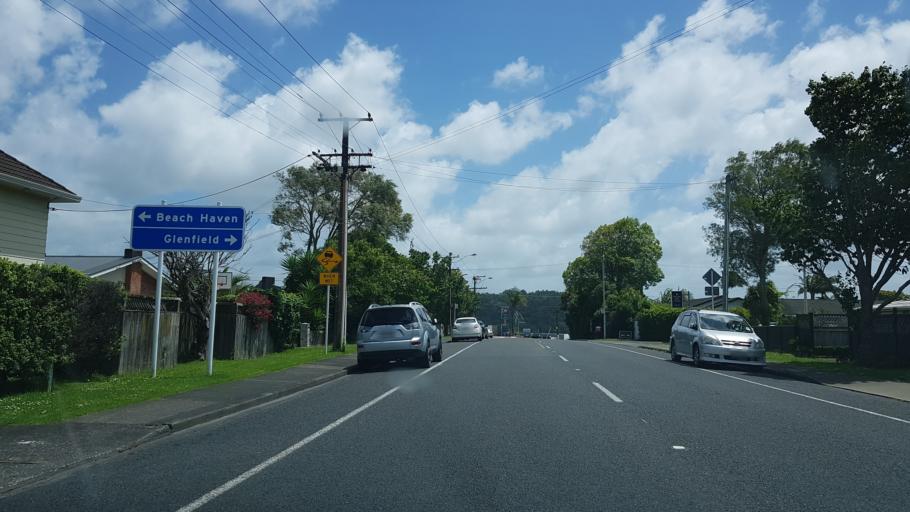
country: NZ
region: Auckland
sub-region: Auckland
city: North Shore
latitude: -36.7892
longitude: 174.7000
